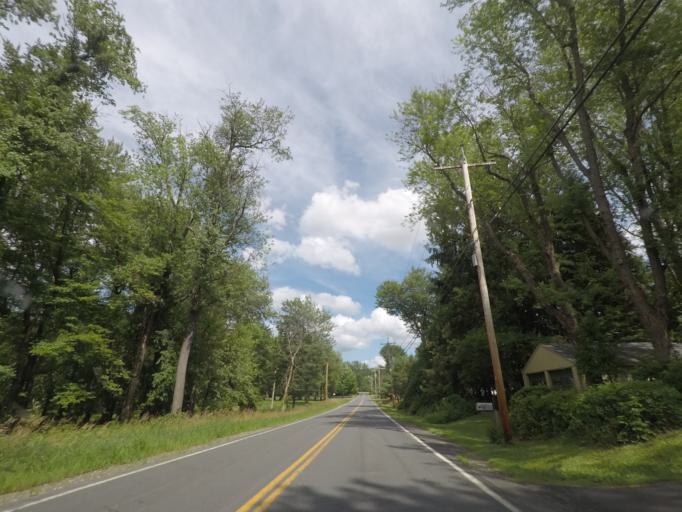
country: US
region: New York
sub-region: Rensselaer County
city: Wynantskill
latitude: 42.7170
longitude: -73.6383
